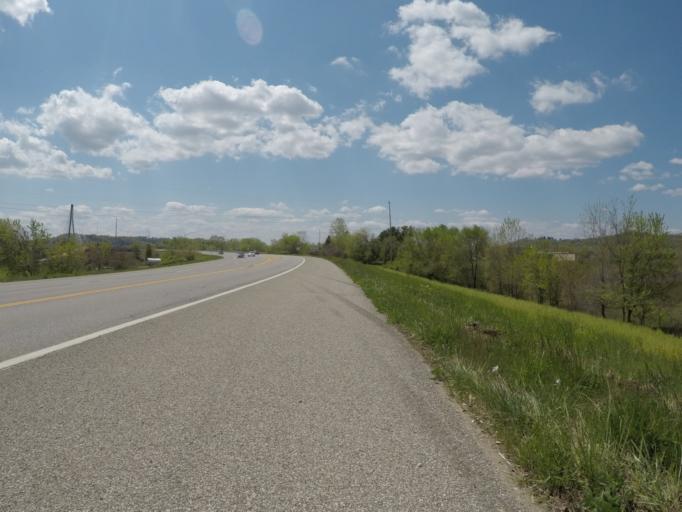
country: US
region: West Virginia
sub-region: Cabell County
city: Huntington
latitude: 38.4426
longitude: -82.3865
